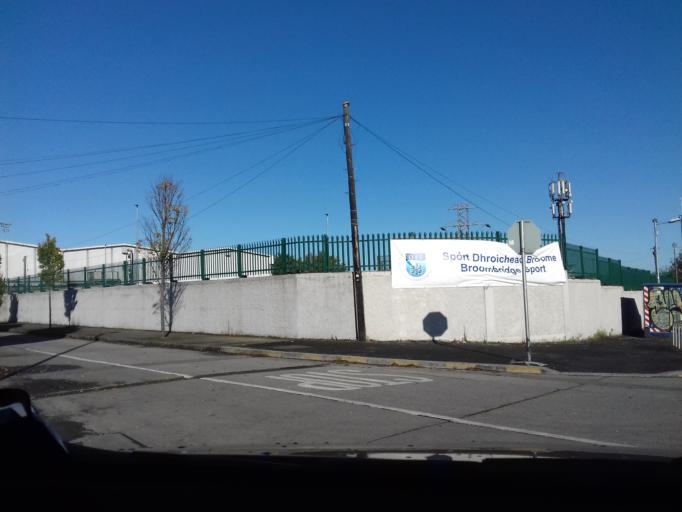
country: IE
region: Leinster
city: Cabra
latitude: 53.3718
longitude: -6.2999
